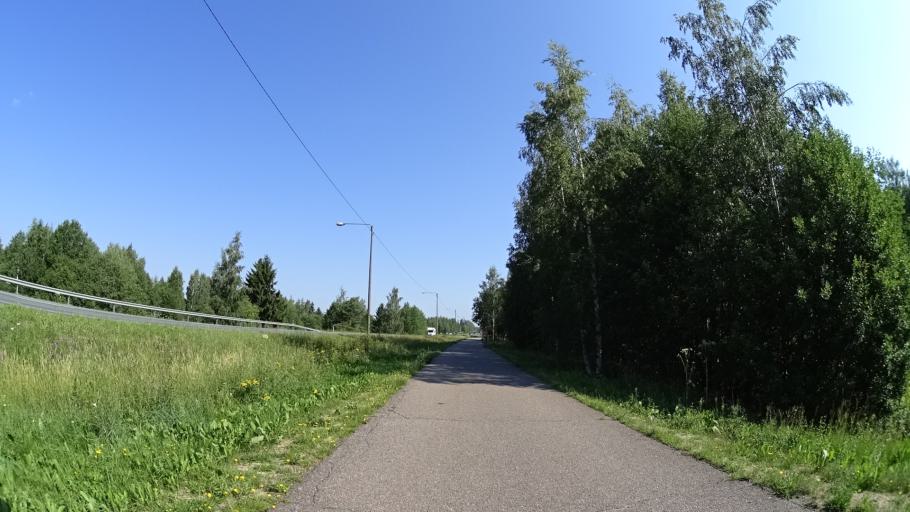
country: FI
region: Uusimaa
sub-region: Helsinki
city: Kerava
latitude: 60.3372
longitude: 25.1250
